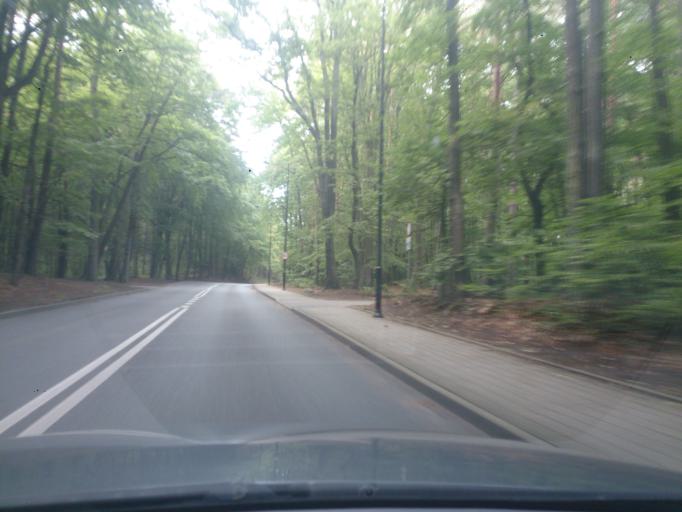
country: PL
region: Pomeranian Voivodeship
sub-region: Sopot
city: Sopot
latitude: 54.4531
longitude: 18.5408
